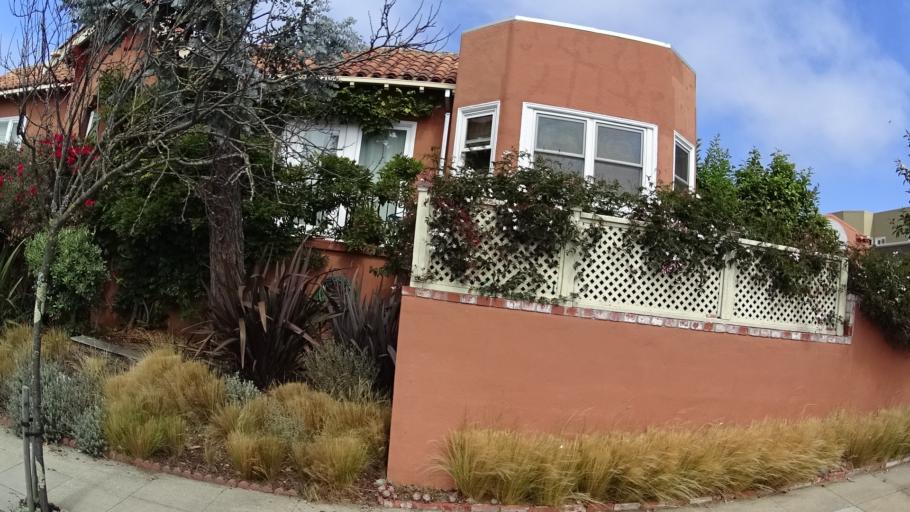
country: US
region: California
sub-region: San Mateo County
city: Daly City
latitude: 37.7318
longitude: -122.4675
